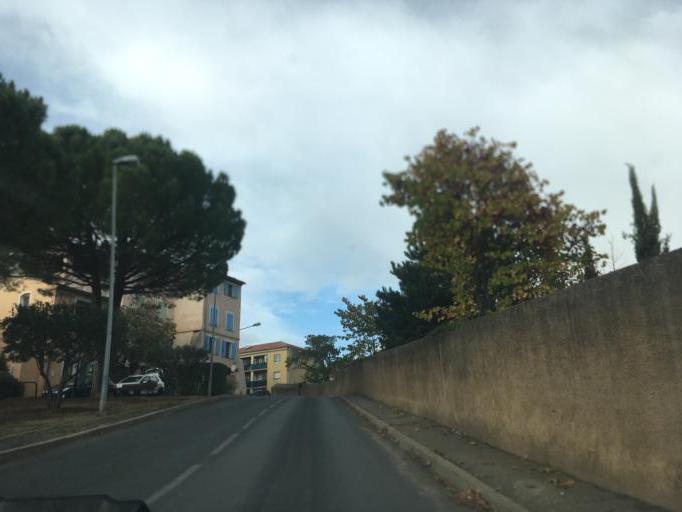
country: FR
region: Provence-Alpes-Cote d'Azur
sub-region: Departement du Var
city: Aups
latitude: 43.6275
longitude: 6.2268
